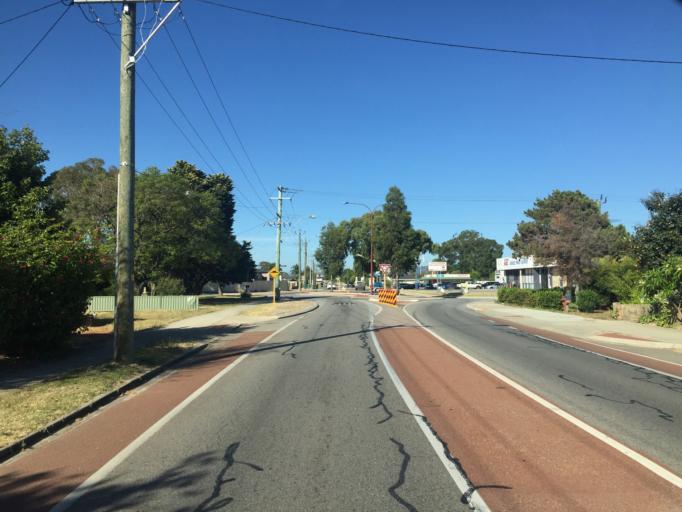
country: AU
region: Western Australia
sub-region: Canning
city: East Cannington
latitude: -32.0147
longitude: 115.9641
